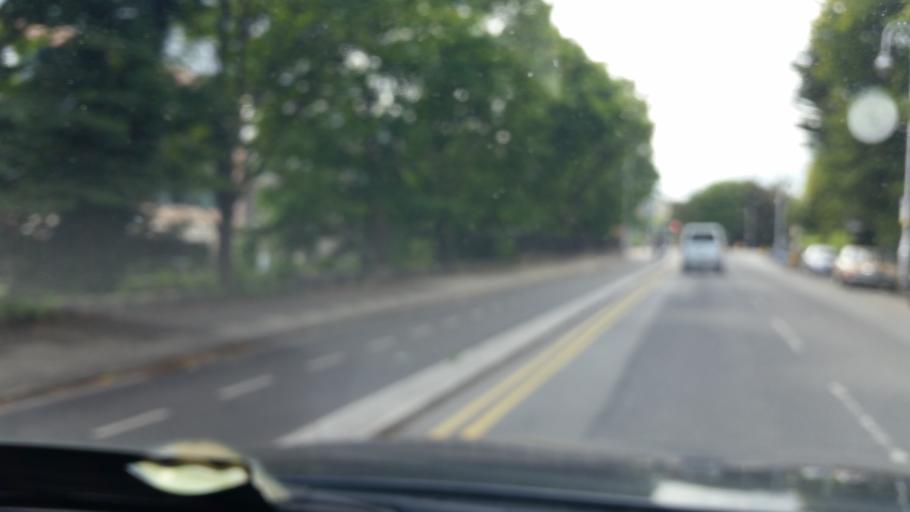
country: IE
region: Leinster
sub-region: Dublin City
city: Dublin
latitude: 53.3352
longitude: -6.2444
